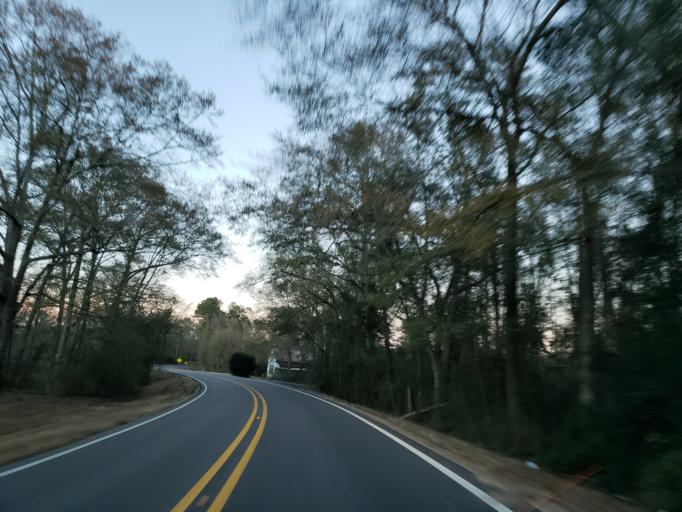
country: US
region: Mississippi
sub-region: Jones County
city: Ellisville
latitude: 31.5767
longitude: -89.2843
